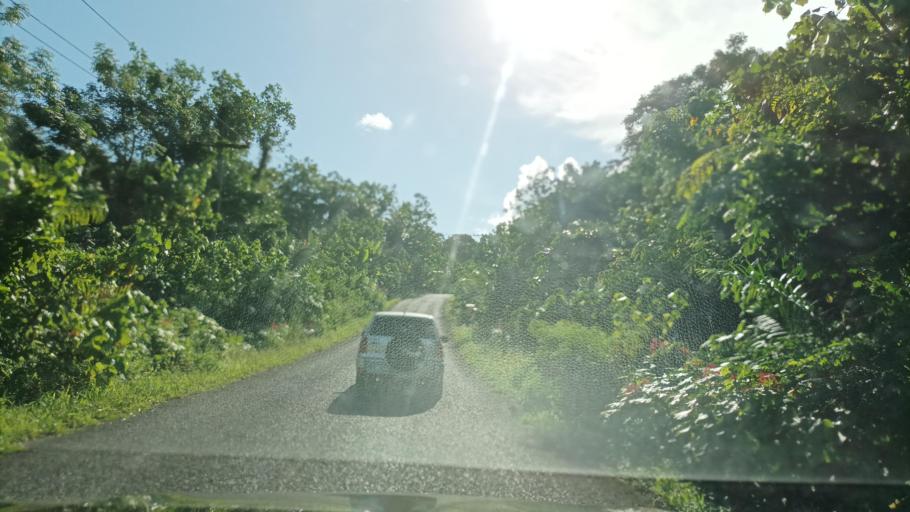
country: FM
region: Pohnpei
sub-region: Sokehs Municipality
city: Palikir - National Government Center
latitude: 6.8201
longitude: 158.1774
